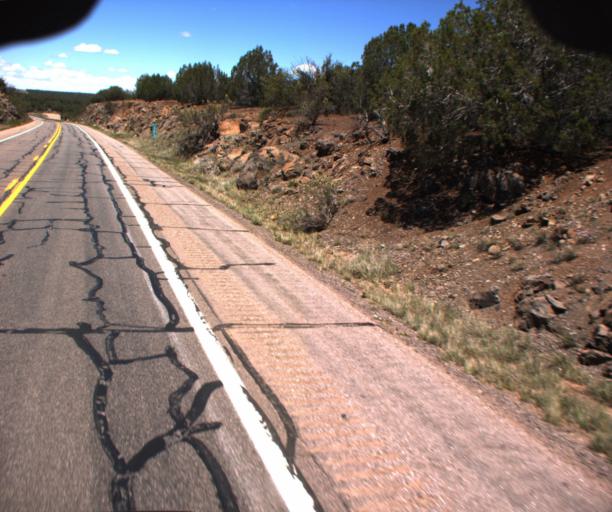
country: US
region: Arizona
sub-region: Yavapai County
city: Paulden
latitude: 35.0777
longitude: -112.4034
